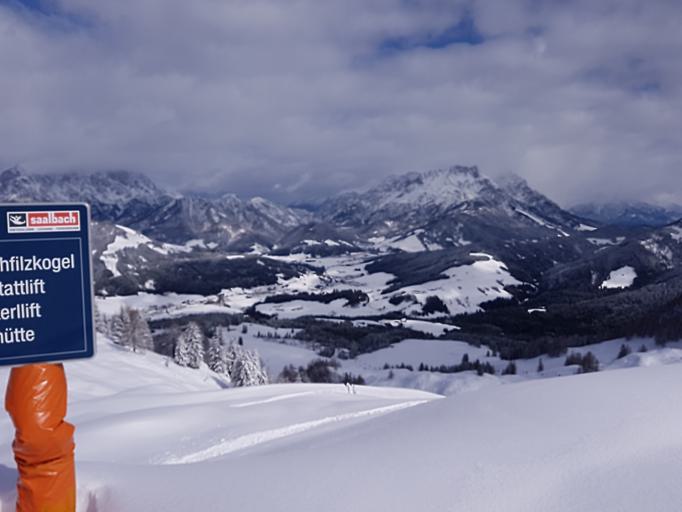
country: AT
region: Tyrol
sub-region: Politischer Bezirk Kitzbuhel
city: Fieberbrunn
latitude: 47.4453
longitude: 12.5502
